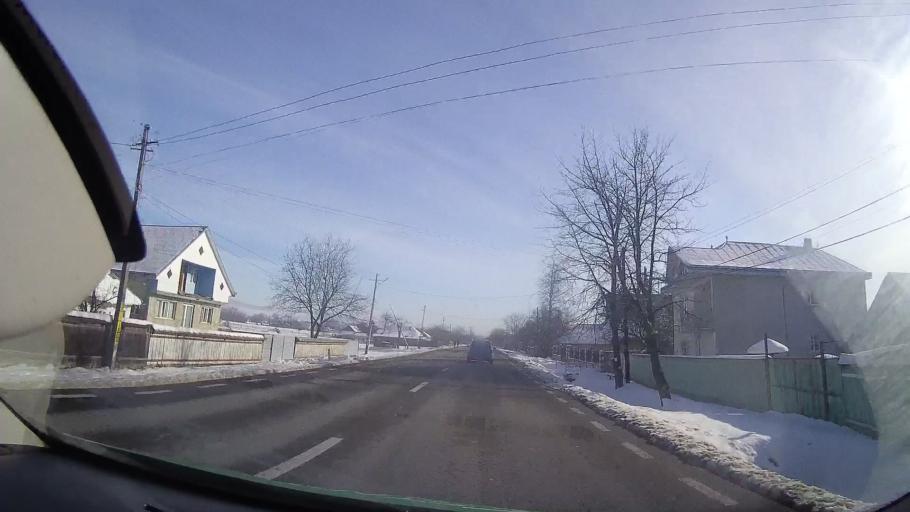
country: RO
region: Neamt
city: Bodesti
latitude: 47.0550
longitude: 26.3960
